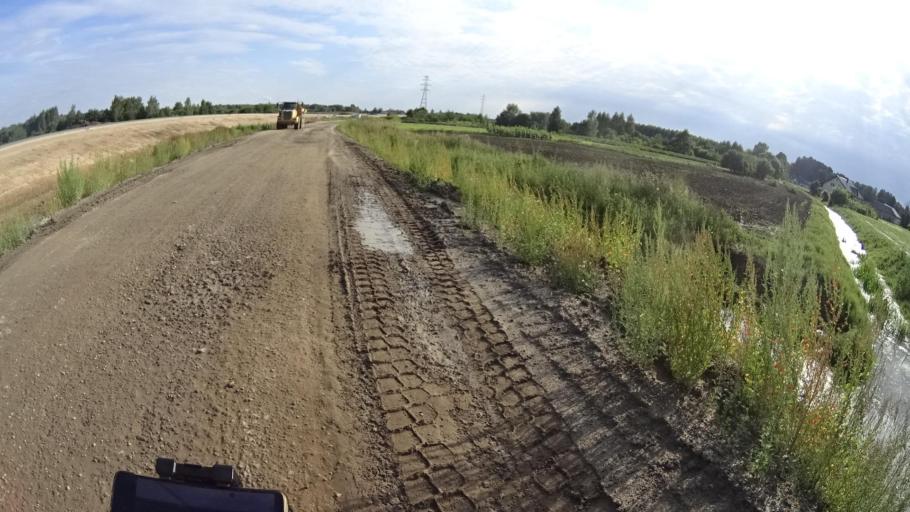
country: PL
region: Masovian Voivodeship
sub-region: Powiat piaseczynski
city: Tarczyn
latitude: 51.9934
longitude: 20.8812
